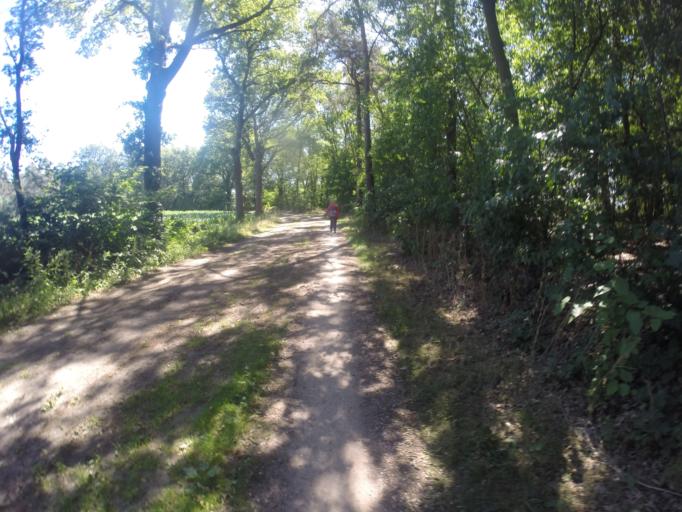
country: NL
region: Gelderland
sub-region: Gemeente Lochem
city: Barchem
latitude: 52.1282
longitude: 6.4307
